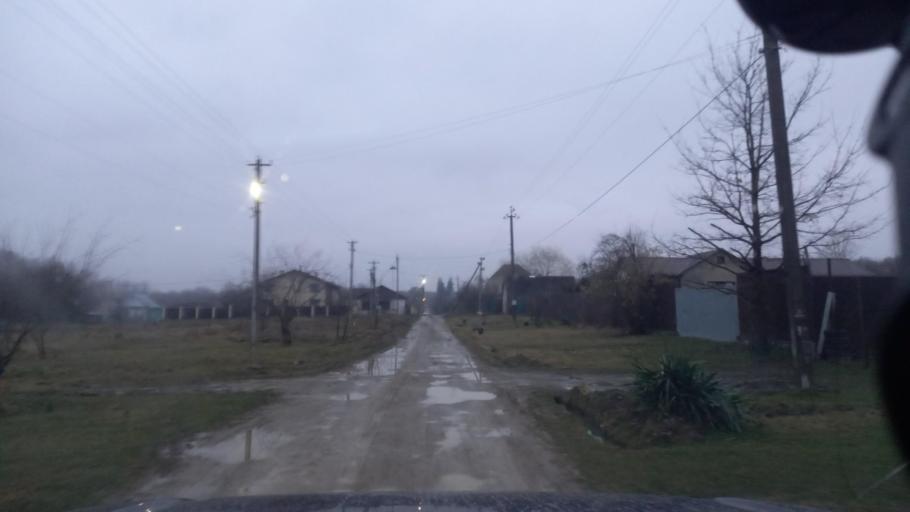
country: RU
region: Krasnodarskiy
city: Saratovskaya
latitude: 44.6474
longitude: 39.3178
